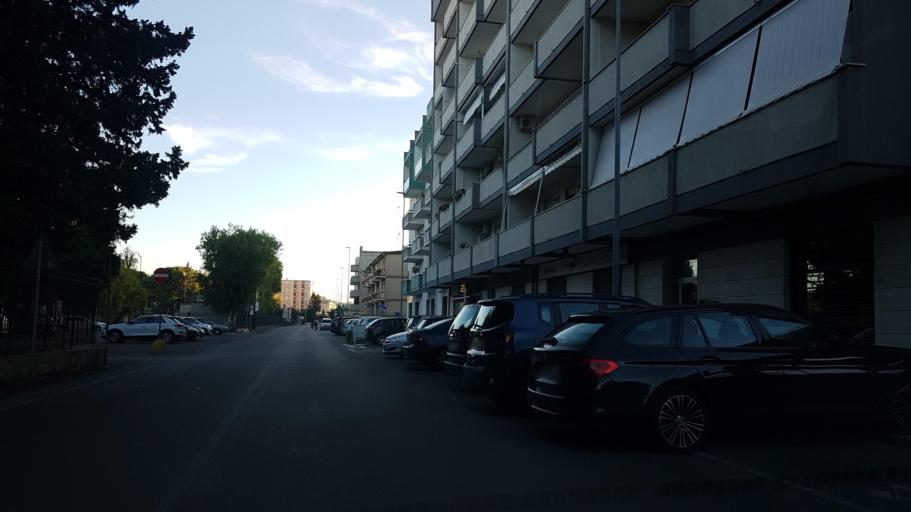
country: IT
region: Apulia
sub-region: Provincia di Lecce
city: Lecce
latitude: 40.3670
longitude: 18.1769
